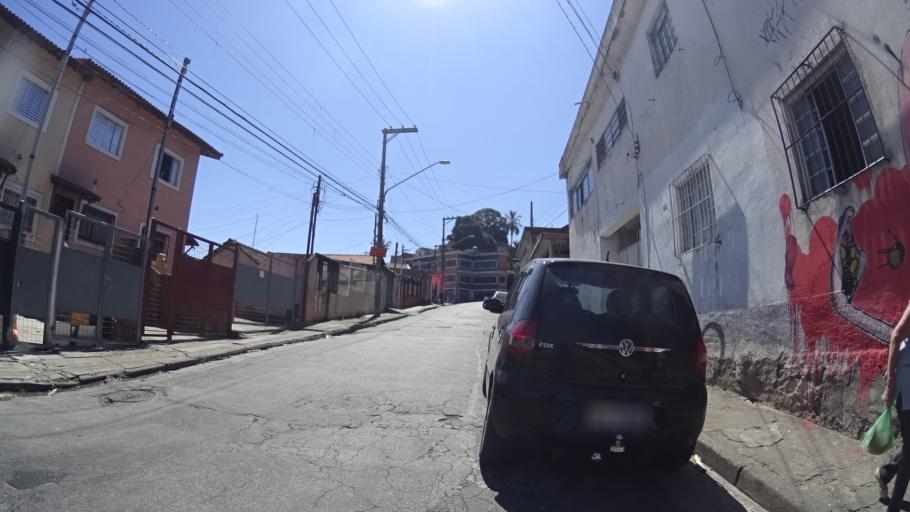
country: BR
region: Sao Paulo
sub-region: Sao Paulo
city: Sao Paulo
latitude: -23.4849
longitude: -46.6709
